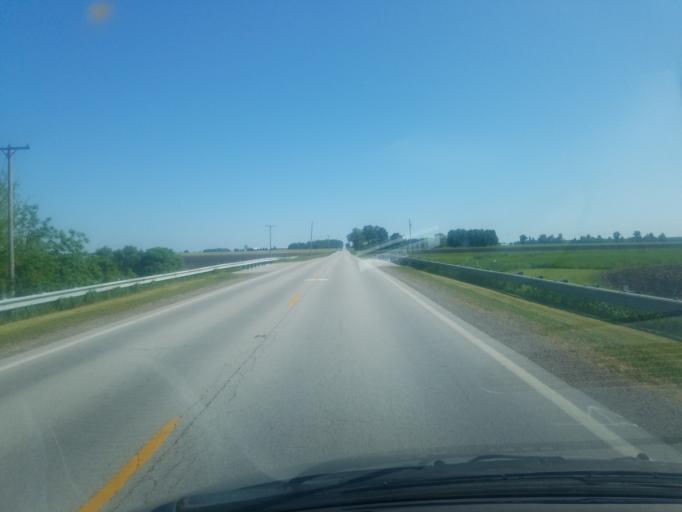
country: US
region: Ohio
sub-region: Huron County
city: Bellevue
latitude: 41.2352
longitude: -82.8085
